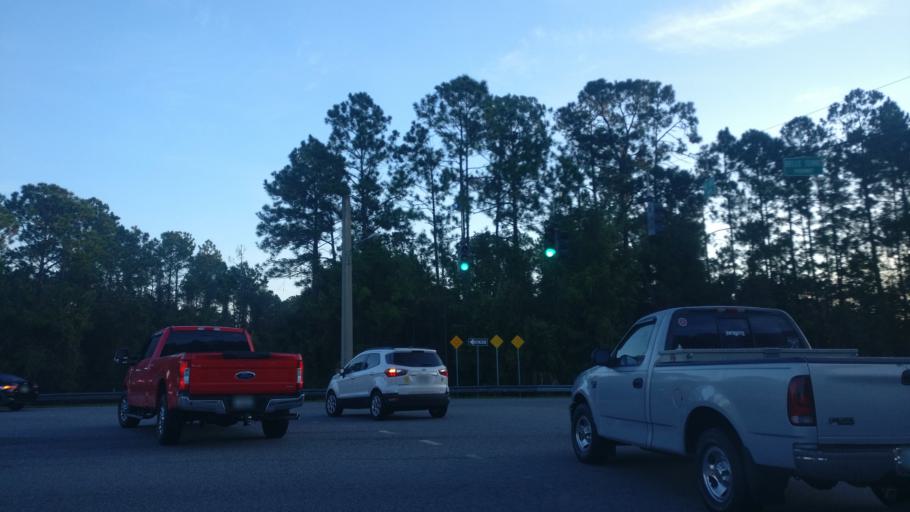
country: US
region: Florida
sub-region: Flagler County
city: Palm Coast
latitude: 29.5456
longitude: -81.2331
